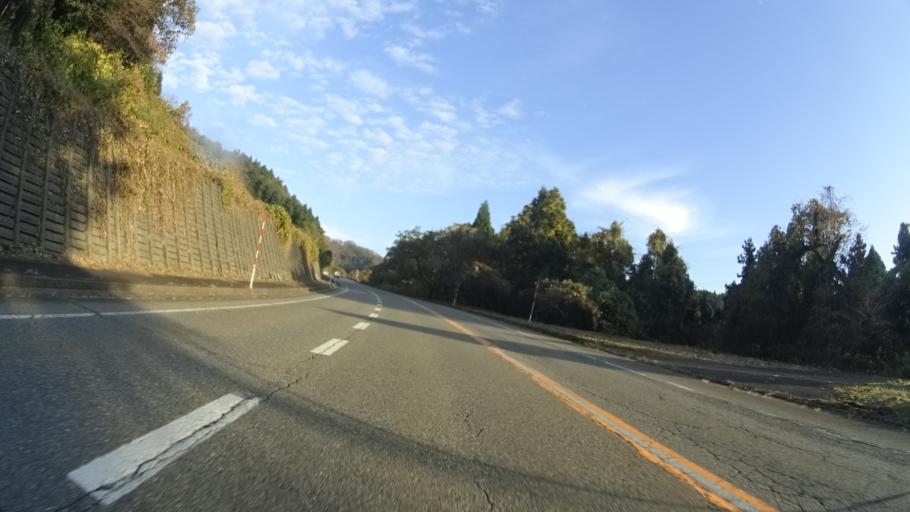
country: JP
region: Niigata
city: Kashiwazaki
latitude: 37.4069
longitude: 138.6477
